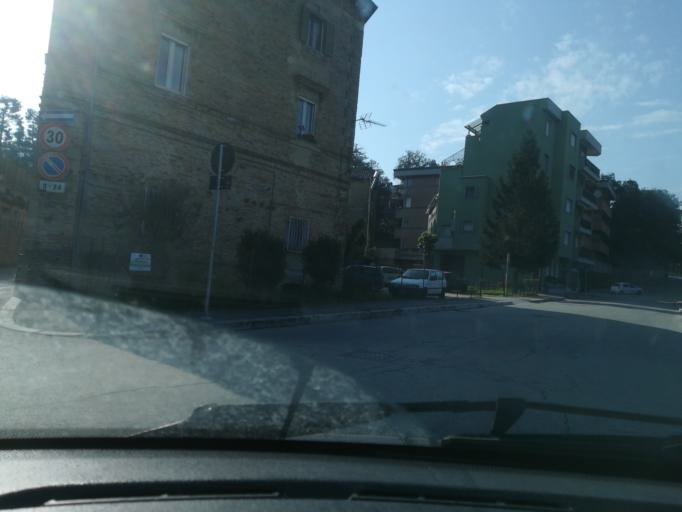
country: IT
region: The Marches
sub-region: Provincia di Macerata
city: Macerata
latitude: 43.2920
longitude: 13.4565
